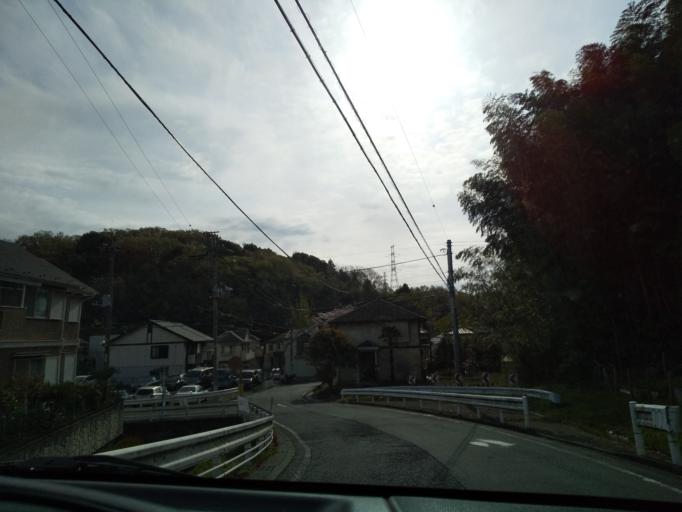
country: JP
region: Tokyo
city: Hino
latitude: 35.6494
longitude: 139.4256
